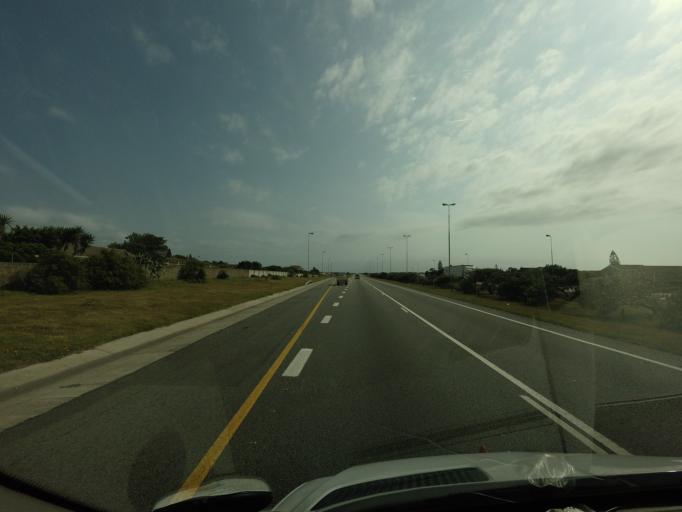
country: ZA
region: Eastern Cape
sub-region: Nelson Mandela Bay Metropolitan Municipality
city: Port Elizabeth
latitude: -33.8571
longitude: 25.6323
